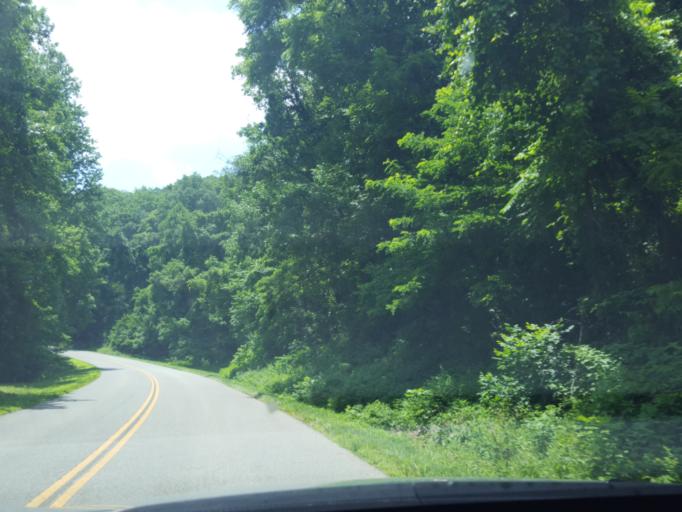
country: US
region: Virginia
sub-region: City of Waynesboro
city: Waynesboro
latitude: 38.0250
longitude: -78.8676
